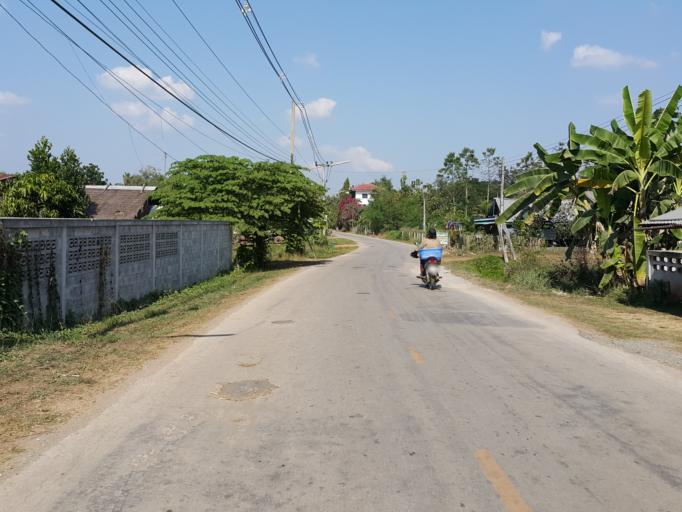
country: TH
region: Sukhothai
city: Thung Saliam
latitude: 17.3293
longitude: 99.5498
